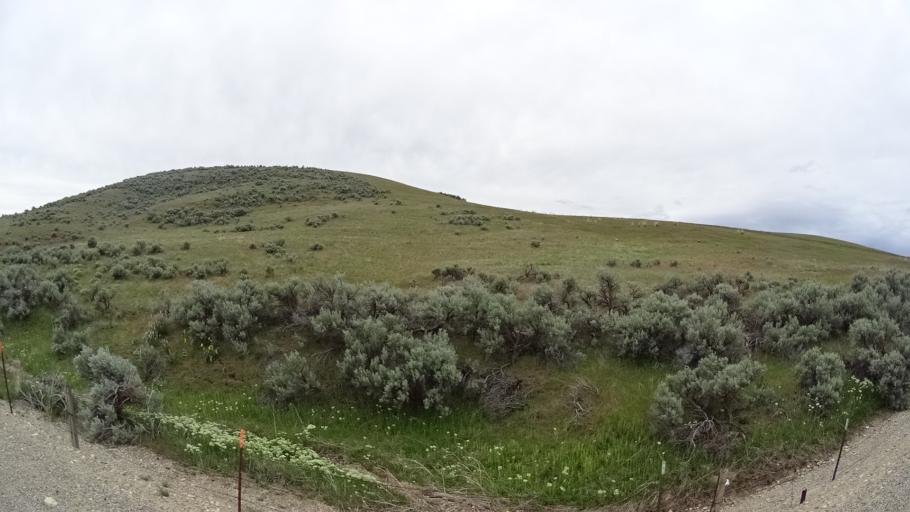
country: US
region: Idaho
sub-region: Ada County
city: Boise
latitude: 43.4880
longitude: -116.0076
